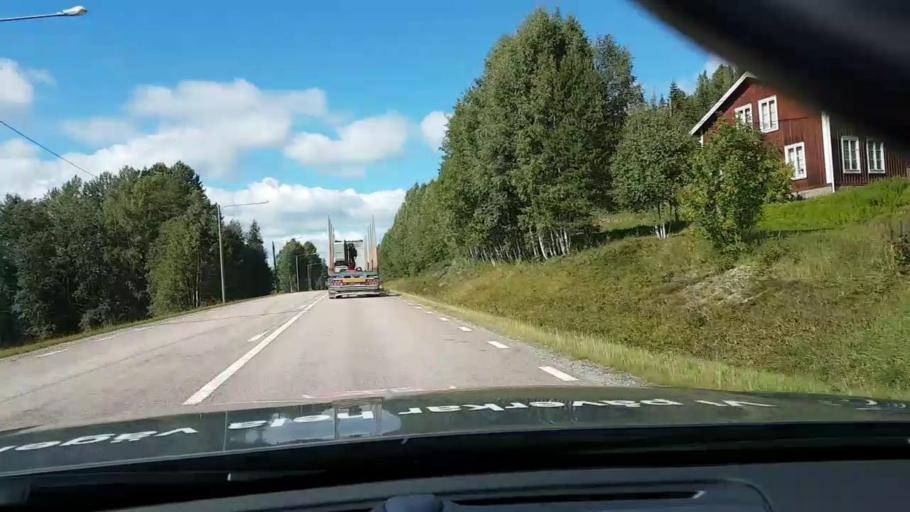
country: SE
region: Vaesternorrland
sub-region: OErnskoeldsviks Kommun
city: Bjasta
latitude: 63.3831
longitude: 18.4004
